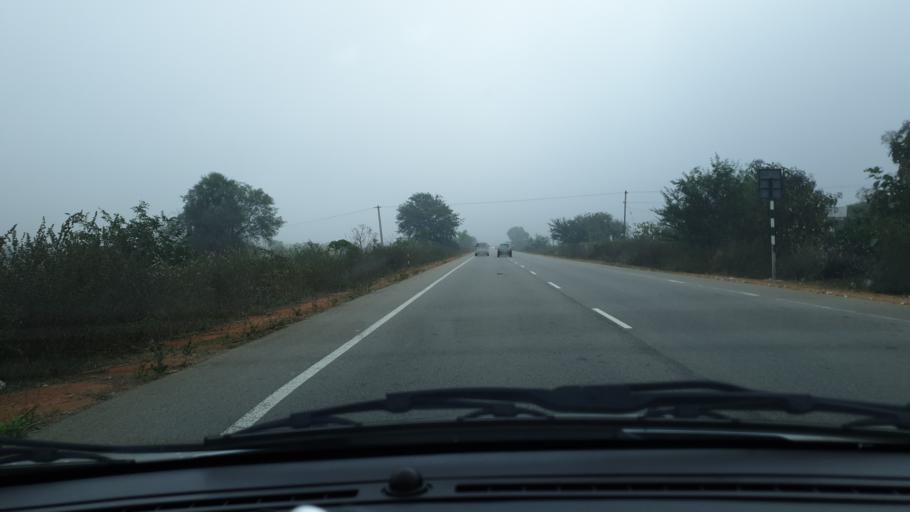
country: IN
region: Telangana
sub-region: Nalgonda
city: Devarkonda
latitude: 16.6302
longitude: 78.6457
